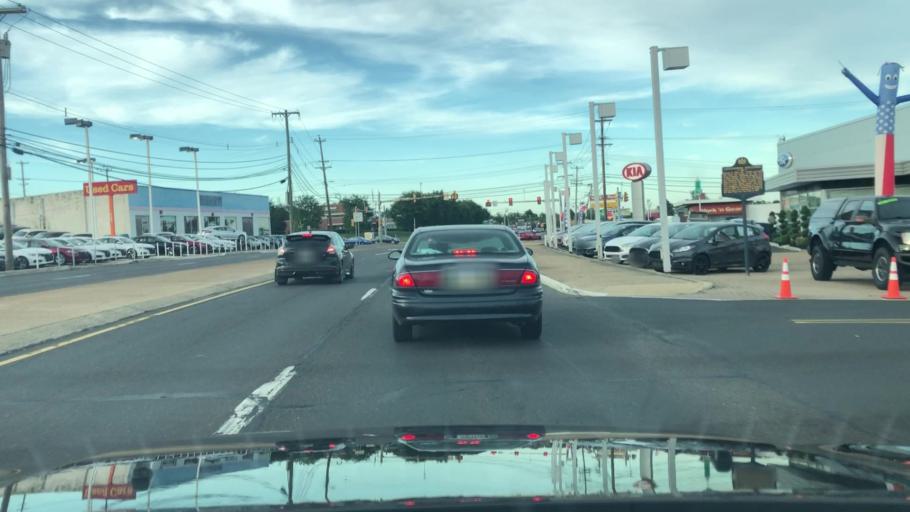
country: US
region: Pennsylvania
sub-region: Bucks County
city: Woodbourne
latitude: 40.1760
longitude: -74.8859
